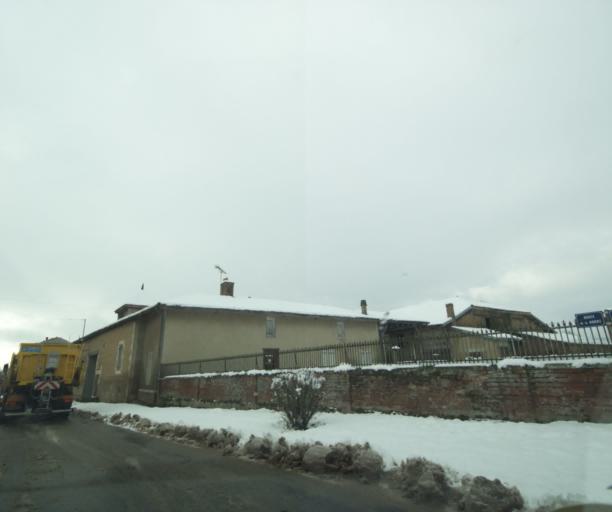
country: FR
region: Champagne-Ardenne
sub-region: Departement de la Haute-Marne
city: Montier-en-Der
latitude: 48.4946
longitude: 4.7011
